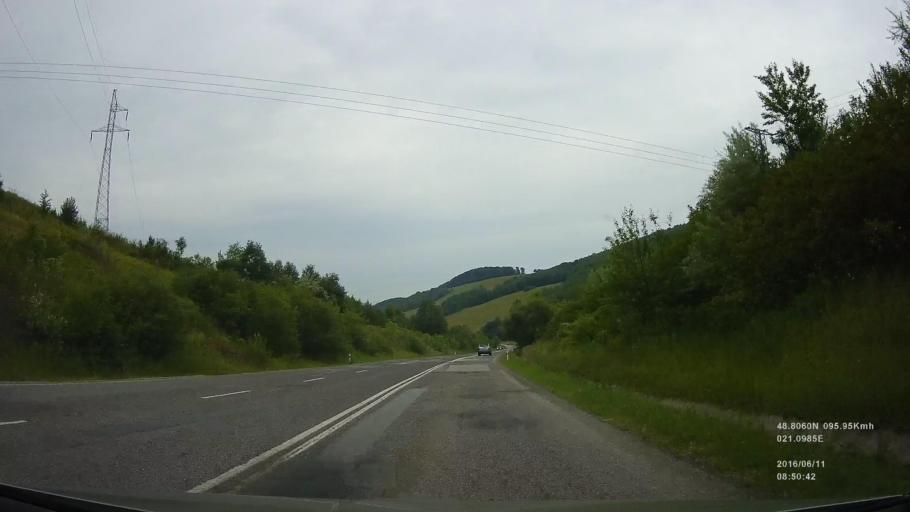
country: SK
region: Kosicky
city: Kosice
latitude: 48.8004
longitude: 21.1075
